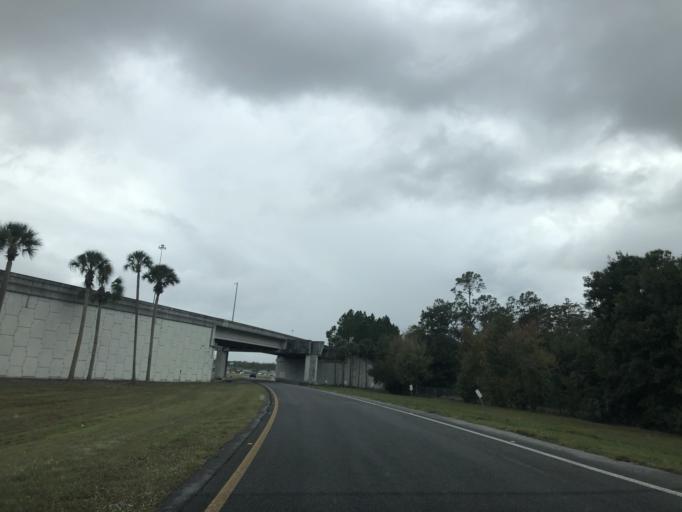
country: US
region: Florida
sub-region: Osceola County
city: Celebration
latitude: 28.3537
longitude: -81.5274
